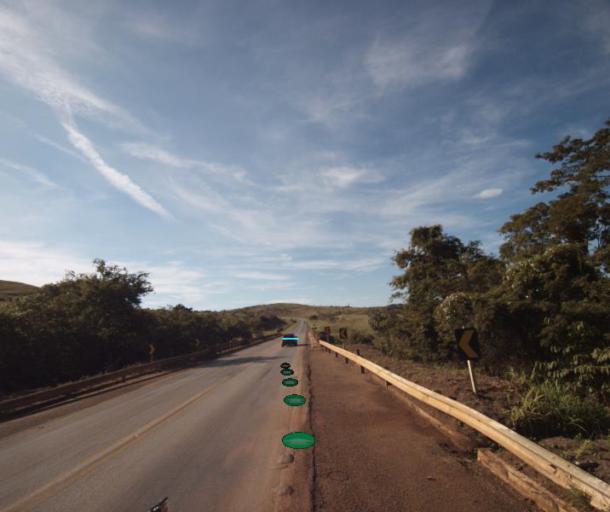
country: BR
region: Federal District
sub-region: Brasilia
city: Brasilia
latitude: -15.7486
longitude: -48.3517
